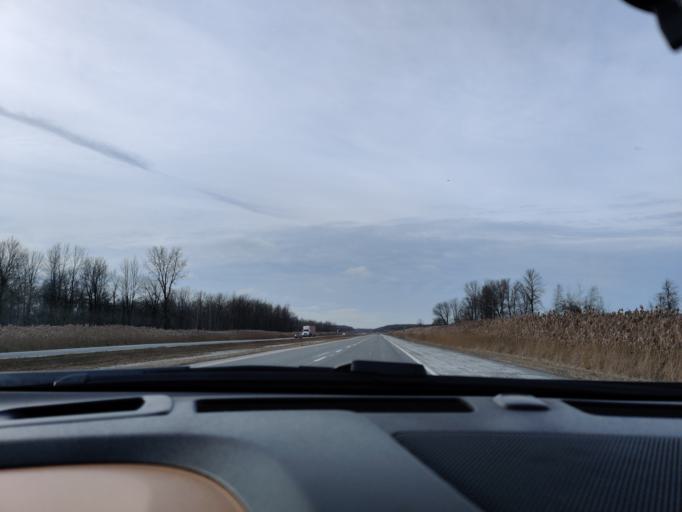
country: CA
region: Quebec
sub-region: Monteregie
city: Les Coteaux
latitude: 45.2405
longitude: -74.2778
